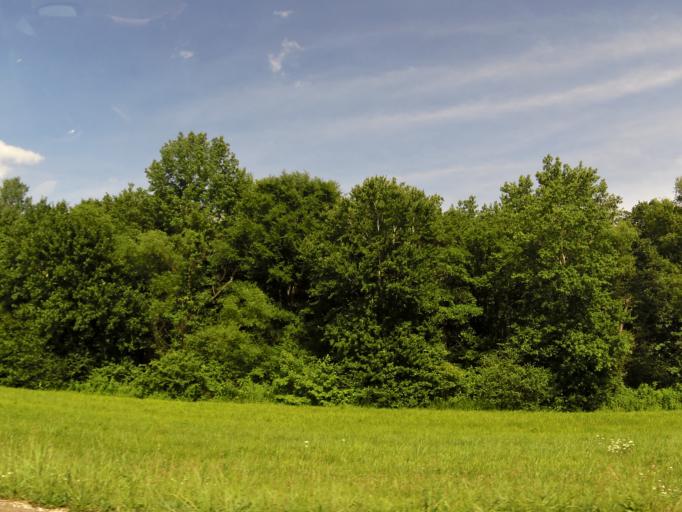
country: US
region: Tennessee
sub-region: Carroll County
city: Huntingdon
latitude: 36.0061
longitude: -88.4462
